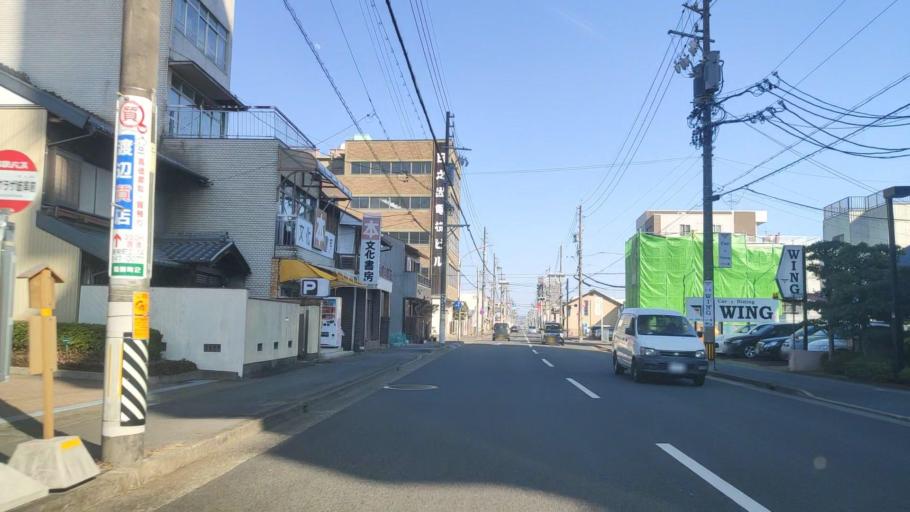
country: JP
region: Gifu
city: Gifu-shi
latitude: 35.4149
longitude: 136.7712
